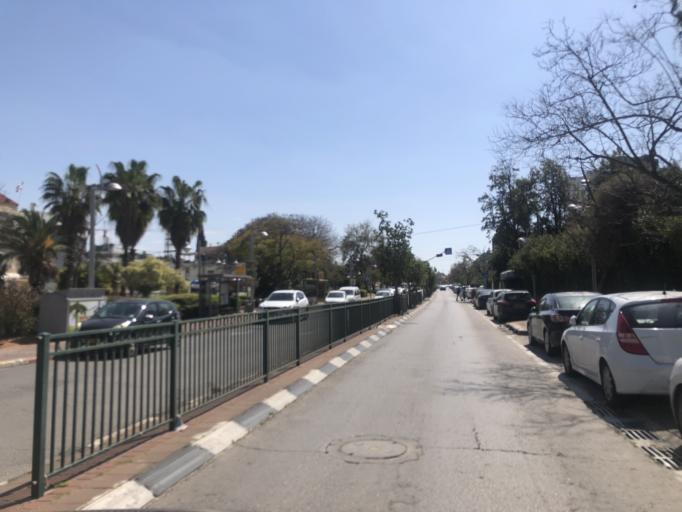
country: IL
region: Tel Aviv
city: Holon
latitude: 32.0130
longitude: 34.7649
